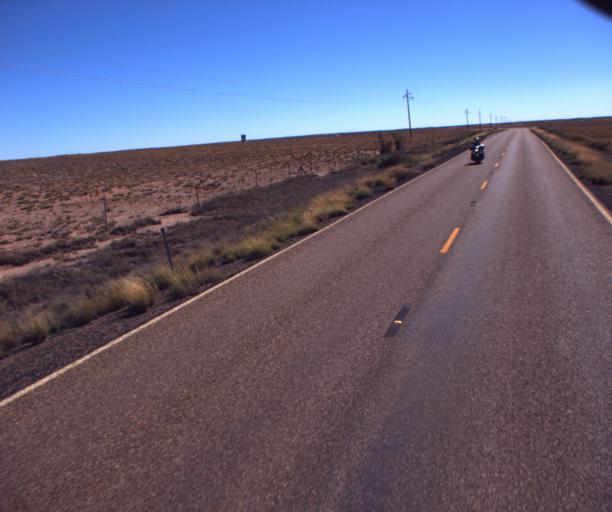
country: US
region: Arizona
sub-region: Navajo County
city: Holbrook
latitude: 35.0747
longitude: -110.0997
